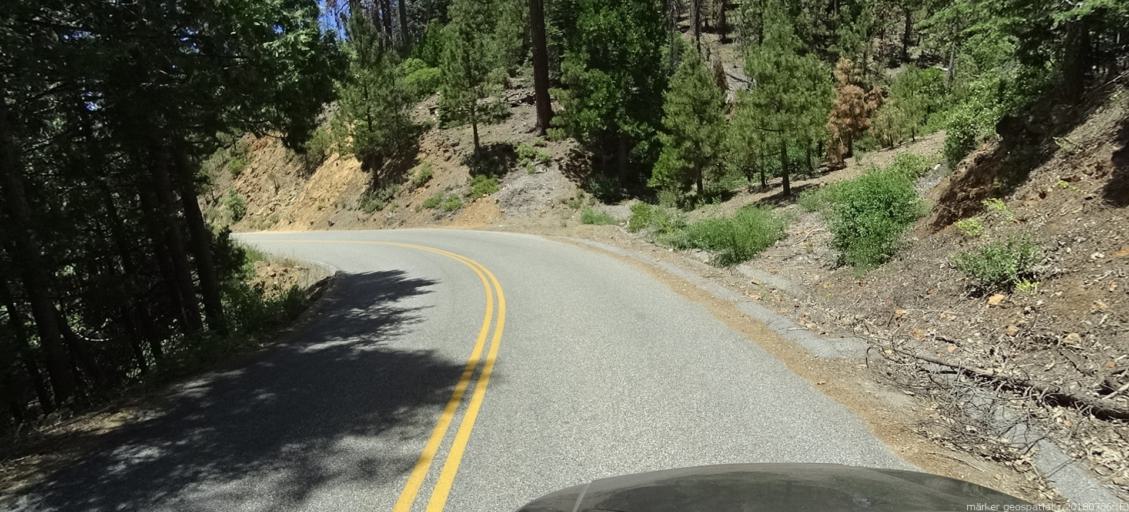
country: US
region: California
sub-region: Madera County
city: Oakhurst
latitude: 37.3800
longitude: -119.5267
